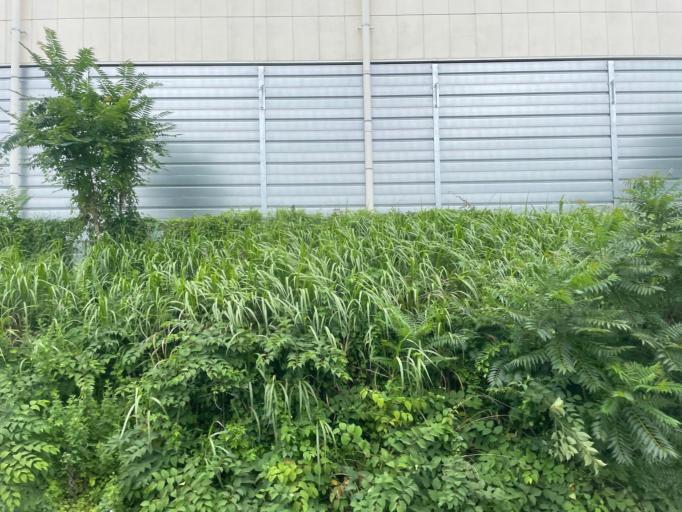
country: JP
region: Gunma
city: Numata
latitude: 36.6374
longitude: 139.0391
